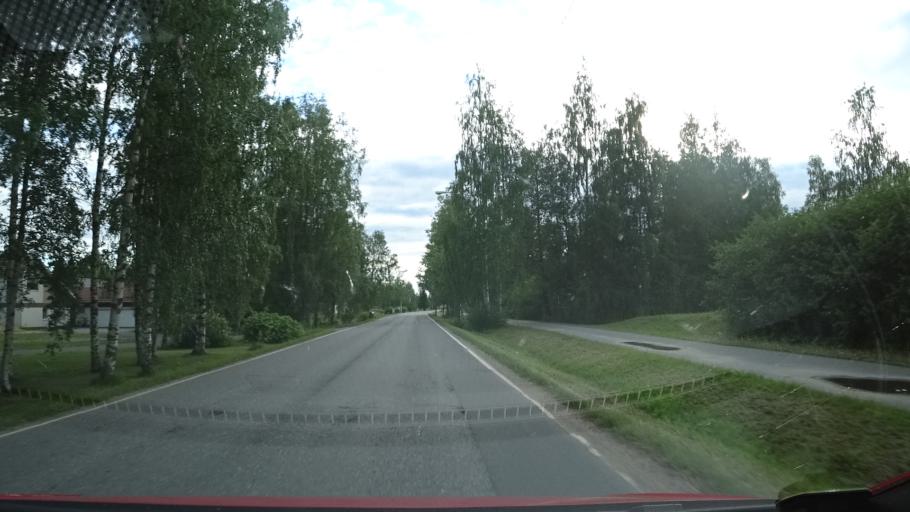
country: FI
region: Northern Ostrobothnia
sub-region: Oulu
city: Liminka
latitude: 64.8080
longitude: 25.4349
